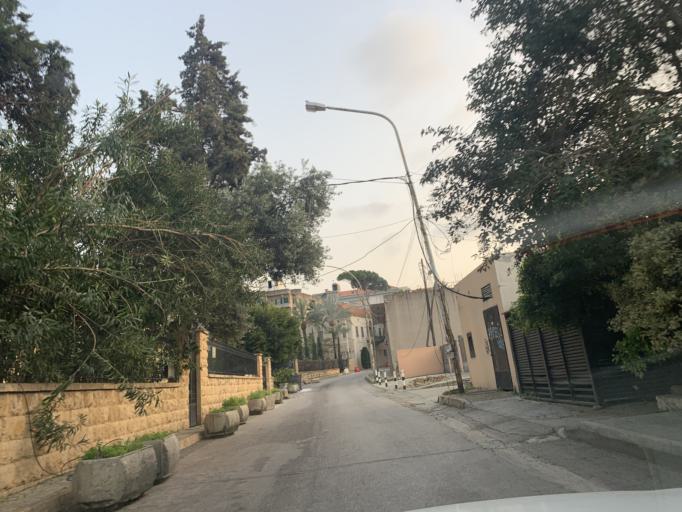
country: LB
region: Mont-Liban
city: Djounie
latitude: 33.9821
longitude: 35.6319
